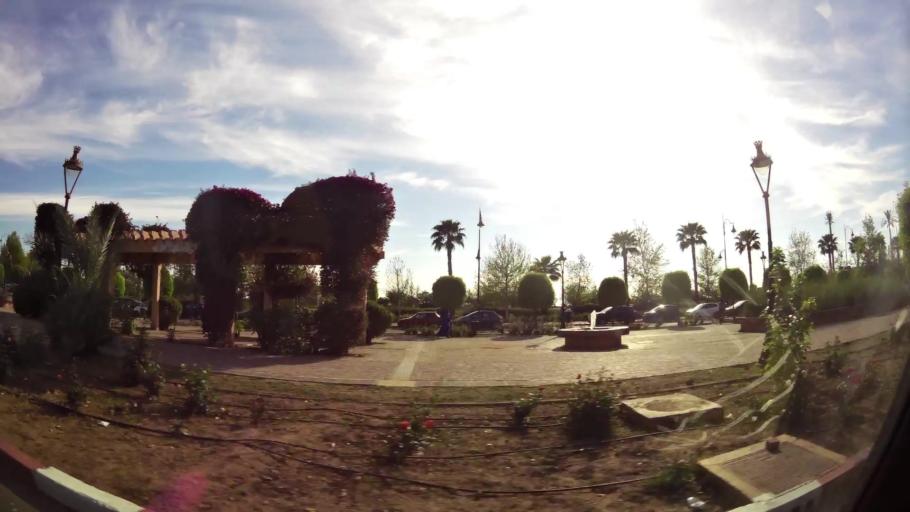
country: MA
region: Marrakech-Tensift-Al Haouz
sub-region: Marrakech
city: Marrakesh
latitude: 31.6166
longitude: -8.0071
